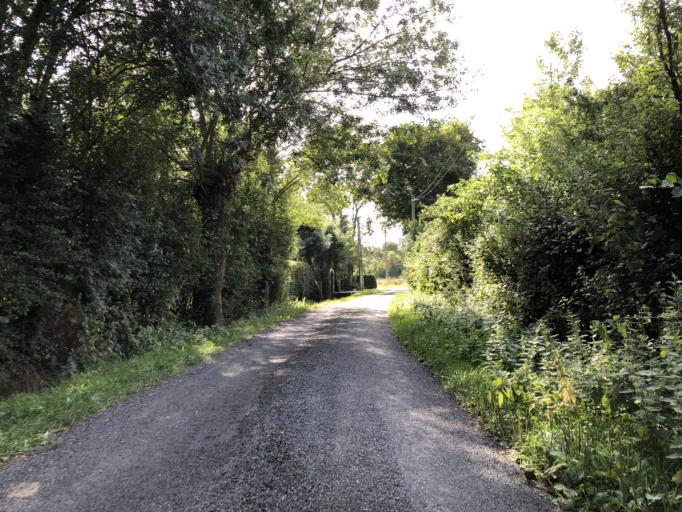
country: FR
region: Pays de la Loire
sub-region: Departement de la Sarthe
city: Chateau-du-Loir
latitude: 47.6821
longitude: 0.4334
